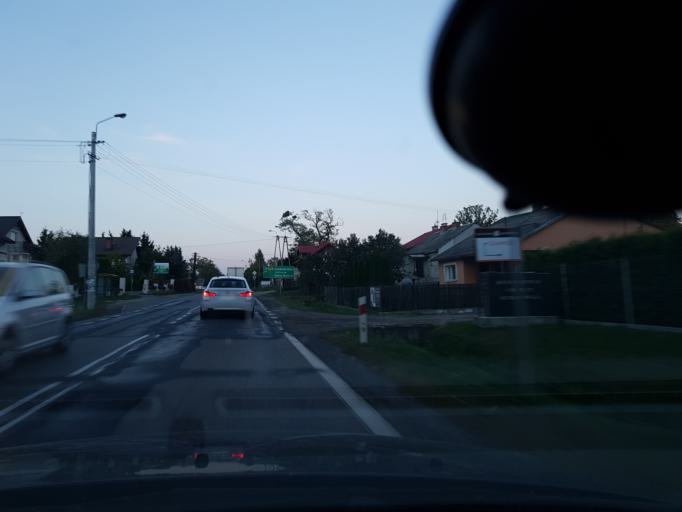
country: PL
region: Masovian Voivodeship
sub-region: Powiat zyrardowski
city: Radziejowice
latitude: 52.0454
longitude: 20.5920
